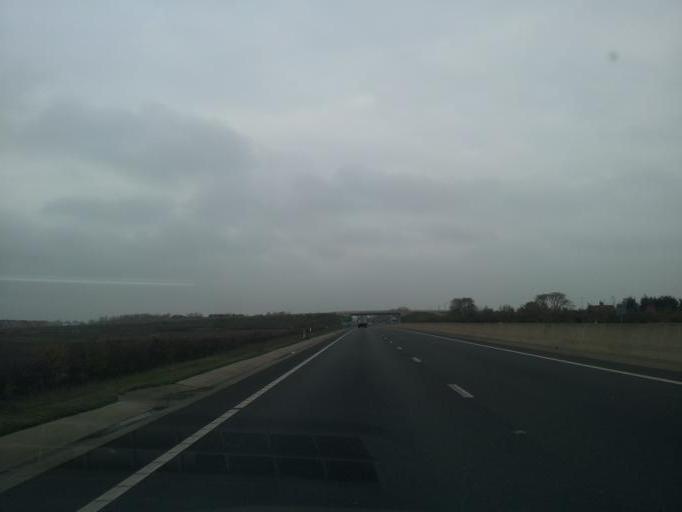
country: GB
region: England
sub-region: Bedford
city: Wootton
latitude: 52.0895
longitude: -0.5182
